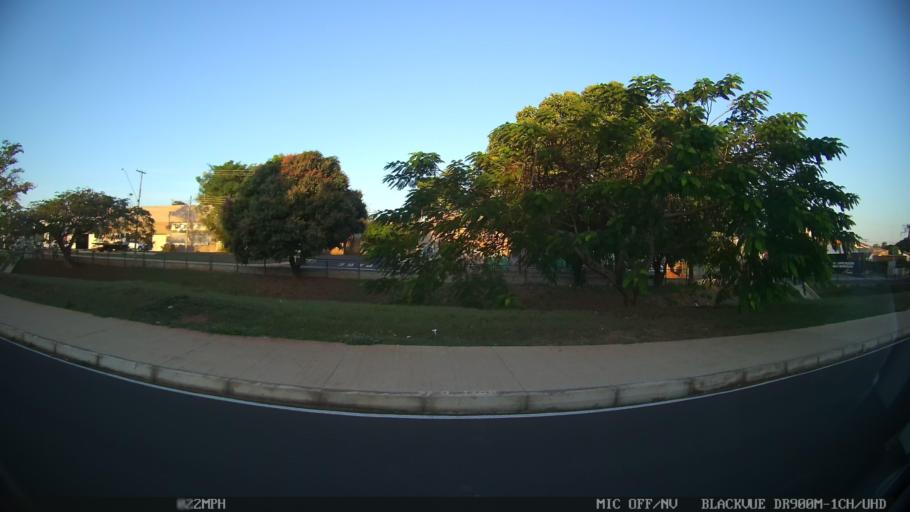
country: BR
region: Sao Paulo
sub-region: Sao Jose Do Rio Preto
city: Sao Jose do Rio Preto
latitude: -20.8053
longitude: -49.3608
